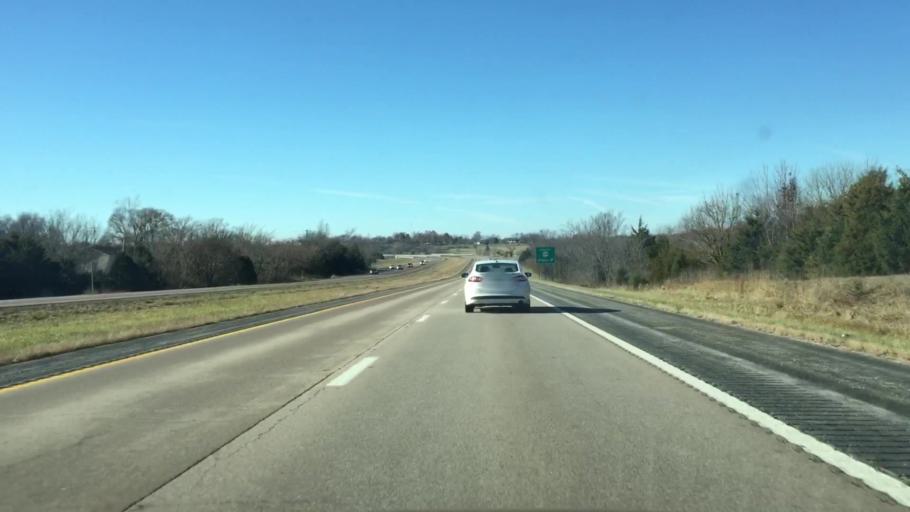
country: US
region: Missouri
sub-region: Miller County
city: Eldon
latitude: 38.3663
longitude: -92.5377
